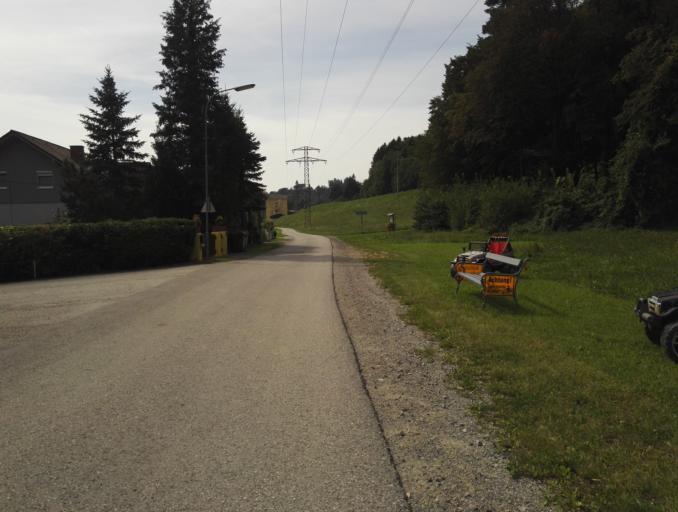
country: AT
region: Styria
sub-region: Politischer Bezirk Graz-Umgebung
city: Peggau
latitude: 47.2127
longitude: 15.3357
